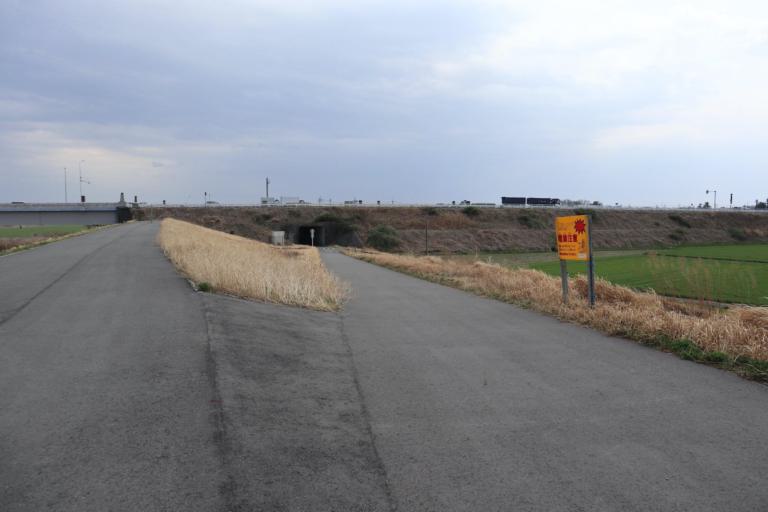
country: JP
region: Gunma
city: Tatebayashi
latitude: 36.2894
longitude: 139.5230
